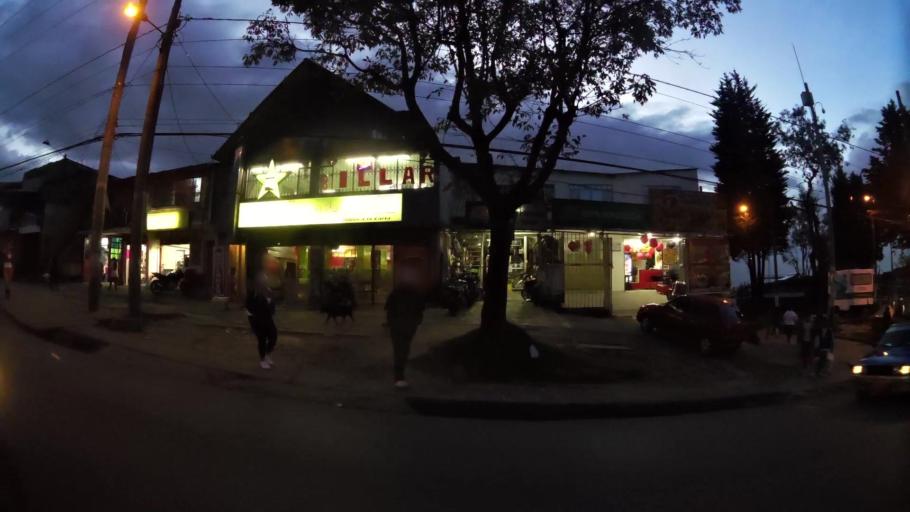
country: CO
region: Bogota D.C.
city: Bogota
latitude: 4.5514
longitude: -74.0863
